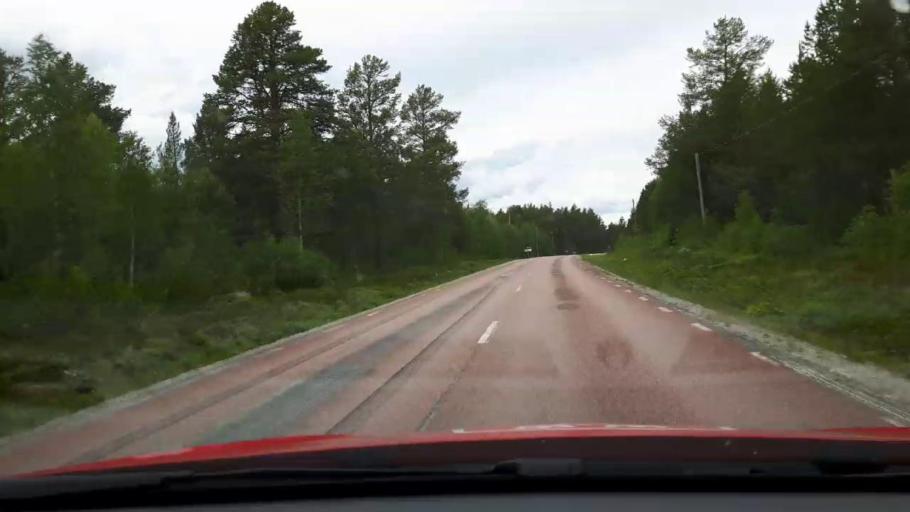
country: NO
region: Hedmark
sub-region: Engerdal
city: Engerdal
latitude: 62.4924
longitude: 12.6390
